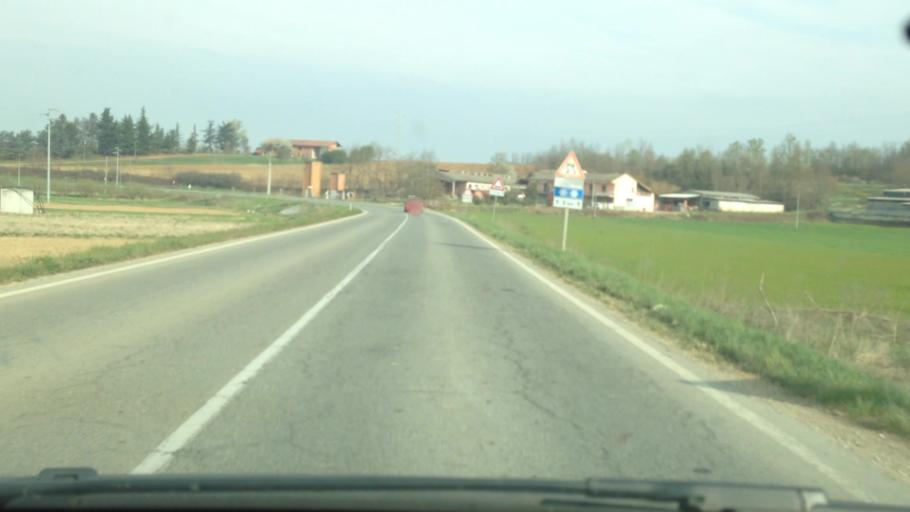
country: IT
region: Piedmont
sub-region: Provincia di Torino
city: Pralormo
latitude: 44.8344
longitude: 7.9240
